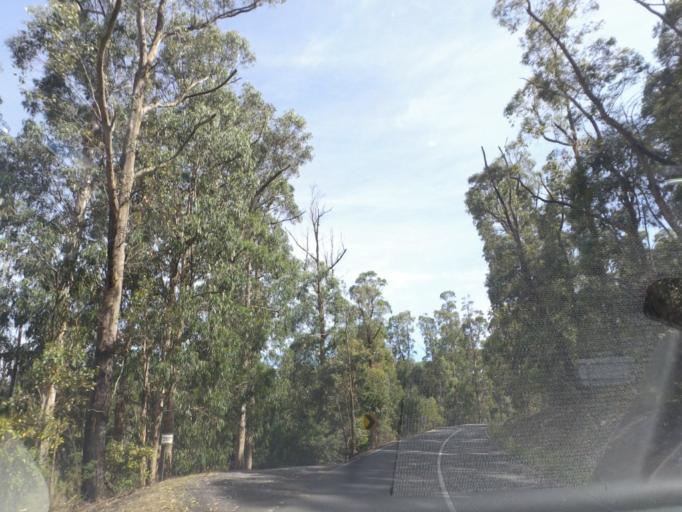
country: AU
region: Victoria
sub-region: Nillumbik
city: Saint Andrews
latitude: -37.5399
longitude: 145.3382
